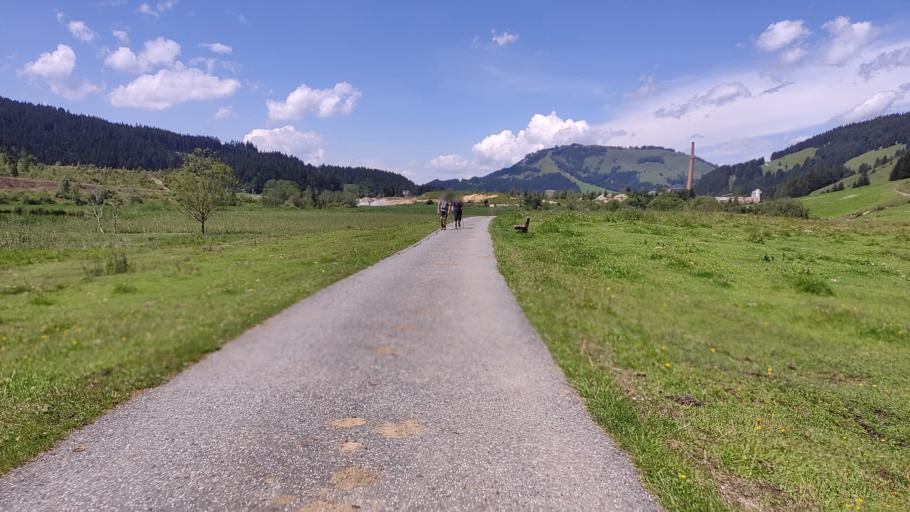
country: AT
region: Tyrol
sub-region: Politischer Bezirk Kitzbuhel
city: Hochfilzen
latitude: 47.4619
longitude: 12.6435
